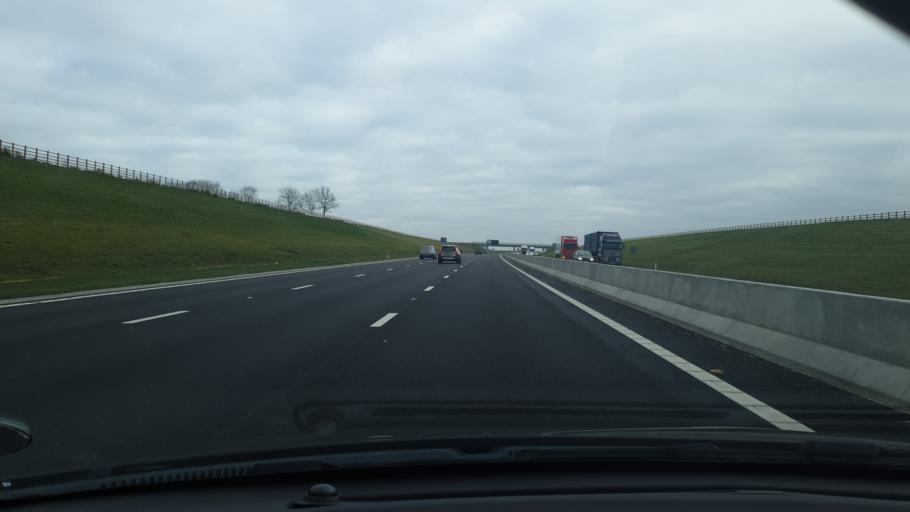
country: GB
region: England
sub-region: Cambridgeshire
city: Godmanchester
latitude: 52.2984
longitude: -0.1944
